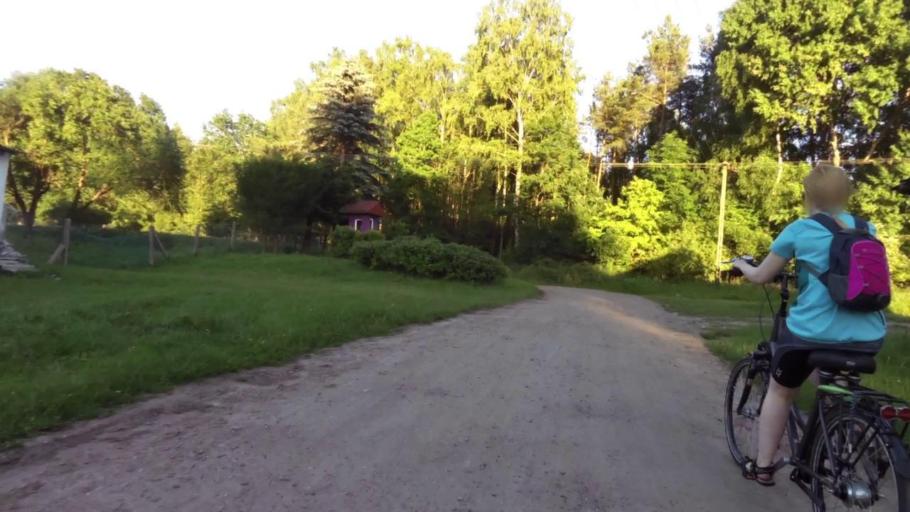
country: PL
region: West Pomeranian Voivodeship
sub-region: Powiat bialogardzki
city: Bialogard
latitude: 54.0616
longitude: 16.1117
